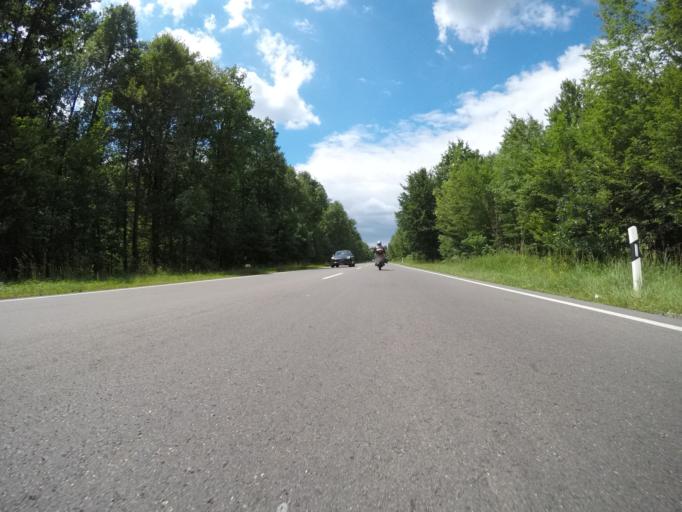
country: DE
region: Baden-Wuerttemberg
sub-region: Regierungsbezirk Stuttgart
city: Gerlingen
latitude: 48.7554
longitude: 9.1081
